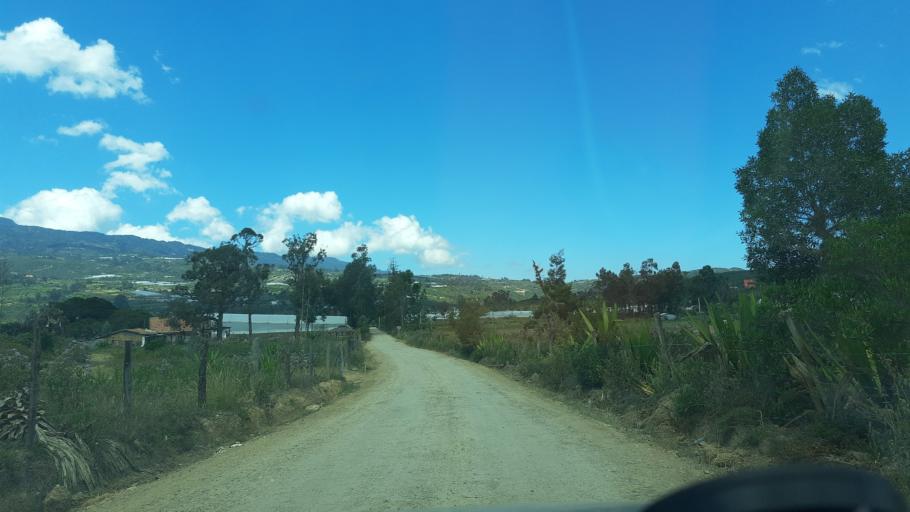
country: CO
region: Boyaca
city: Villa de Leiva
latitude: 5.6631
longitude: -73.5723
